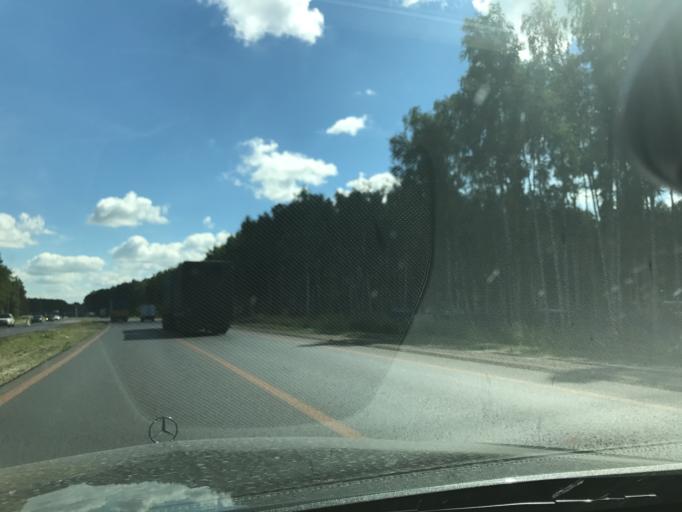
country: RU
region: Nizjnij Novgorod
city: Gorbatovka
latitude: 56.2478
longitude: 43.7158
